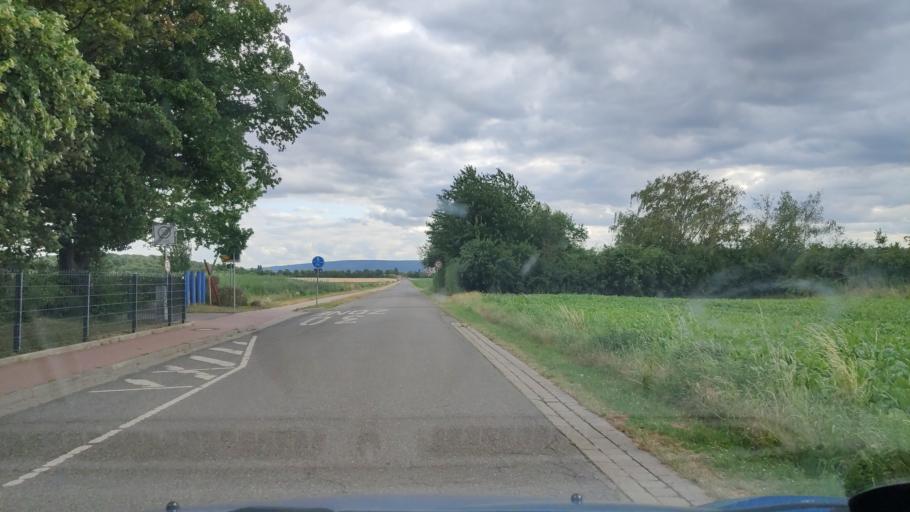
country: DE
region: Lower Saxony
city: Ronnenberg
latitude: 52.3111
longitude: 9.6498
